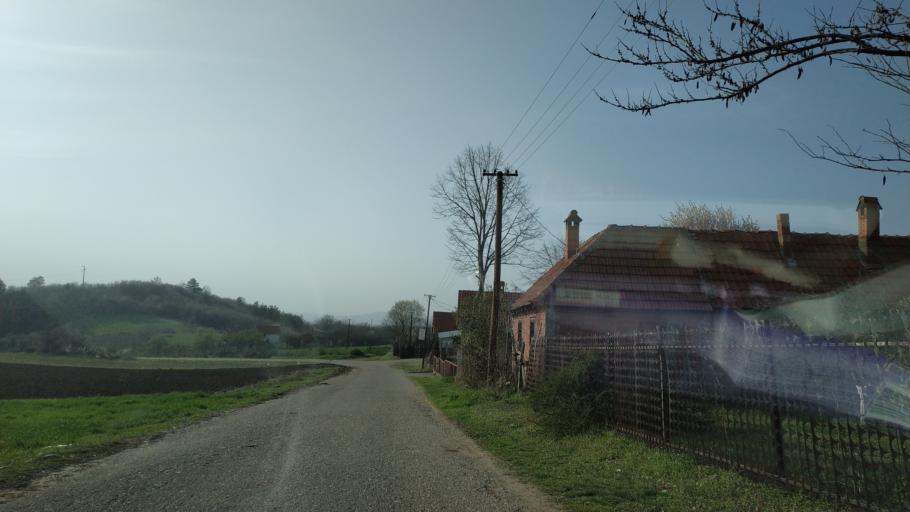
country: RS
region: Central Serbia
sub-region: Nisavski Okrug
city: Aleksinac
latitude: 43.5475
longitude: 21.7244
